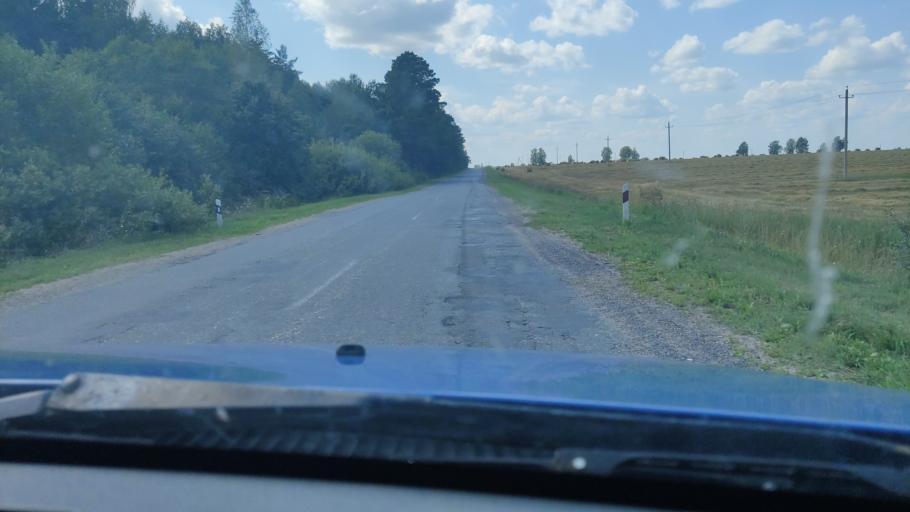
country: BY
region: Vitebsk
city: Dokshytsy
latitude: 54.9240
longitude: 27.8715
